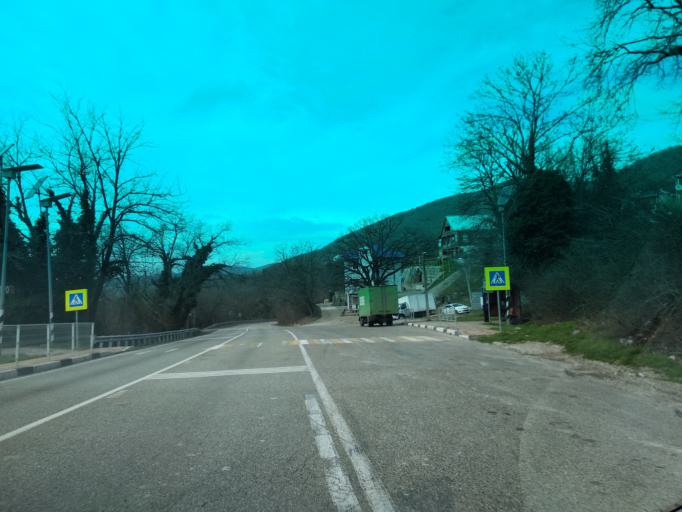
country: RU
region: Krasnodarskiy
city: Tuapse
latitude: 44.0877
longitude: 39.1240
